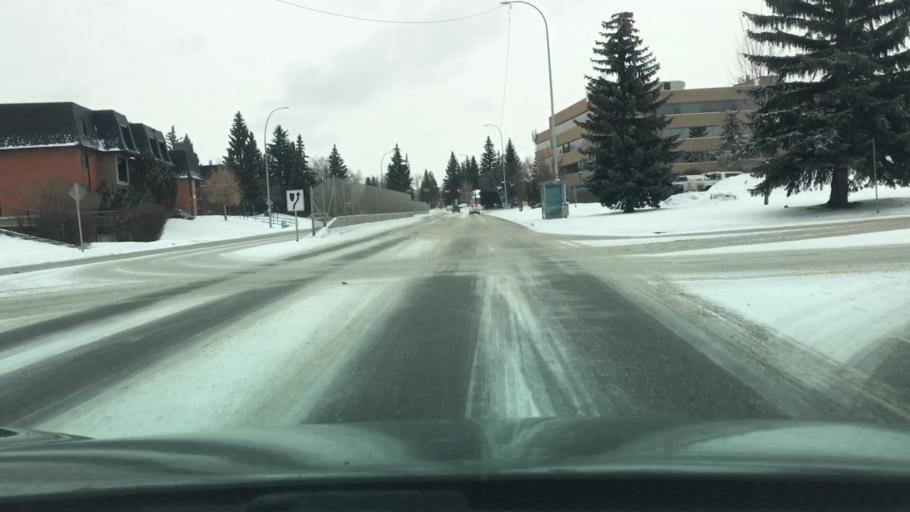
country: CA
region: Alberta
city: Calgary
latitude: 51.0864
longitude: -114.1588
